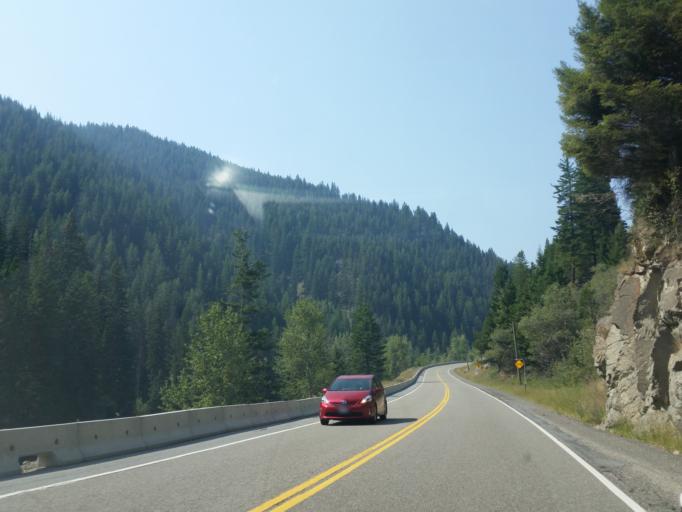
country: CA
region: British Columbia
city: Princeton
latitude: 49.1733
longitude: -120.5544
